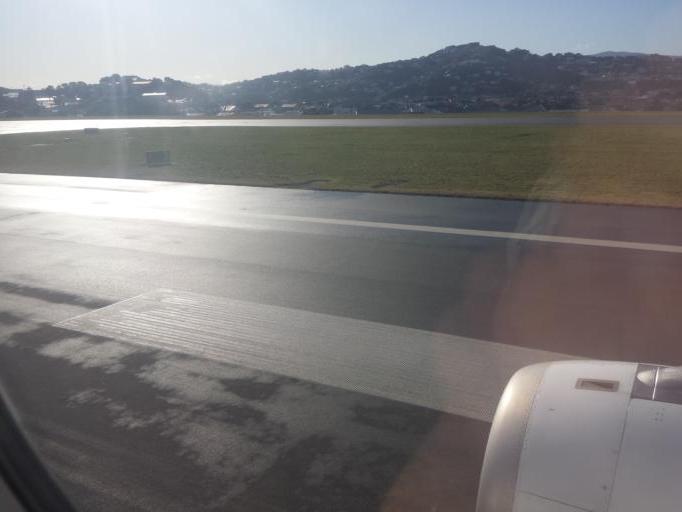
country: NZ
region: Wellington
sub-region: Wellington City
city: Wellington
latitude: -41.3227
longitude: 174.8070
